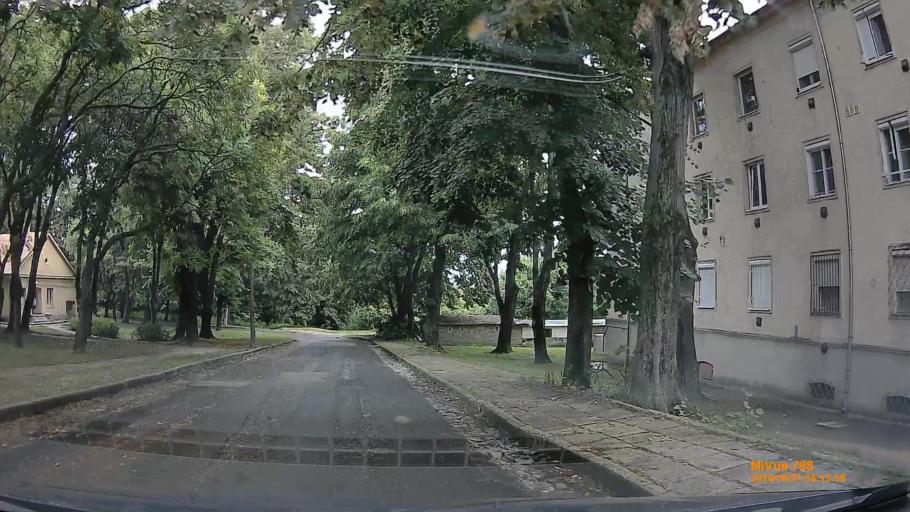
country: HU
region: Baranya
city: Pecs
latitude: 46.0990
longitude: 18.2673
